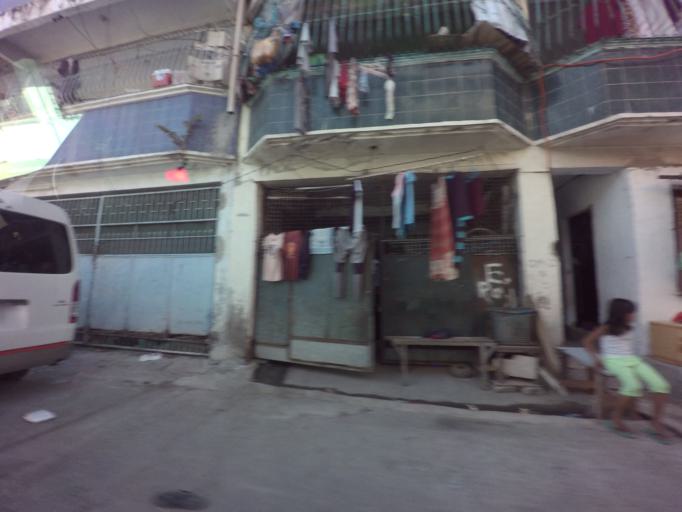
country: PH
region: Calabarzon
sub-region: Province of Rizal
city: Taguig
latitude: 14.4958
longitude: 121.0551
